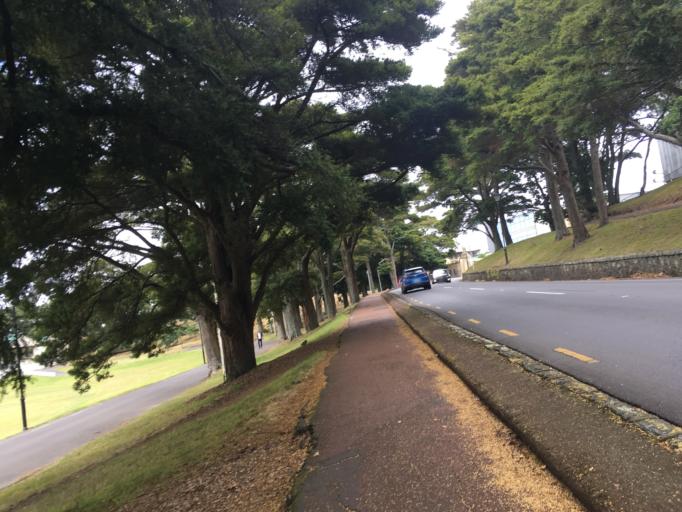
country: NZ
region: Auckland
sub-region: Auckland
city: Auckland
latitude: -36.8612
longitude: 174.7716
